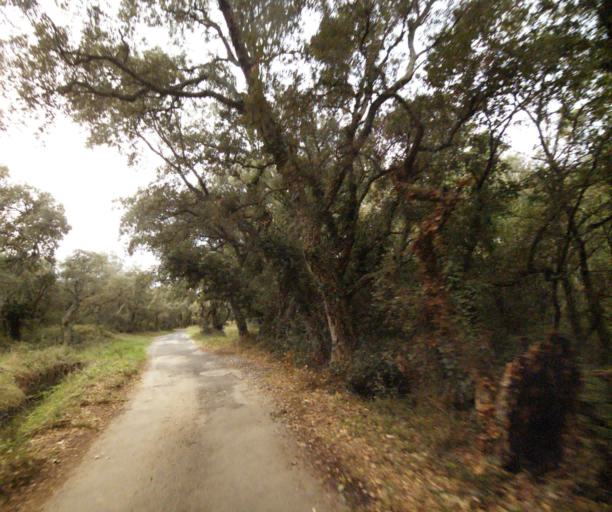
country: FR
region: Languedoc-Roussillon
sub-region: Departement des Pyrenees-Orientales
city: Argelers
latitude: 42.5580
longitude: 3.0217
